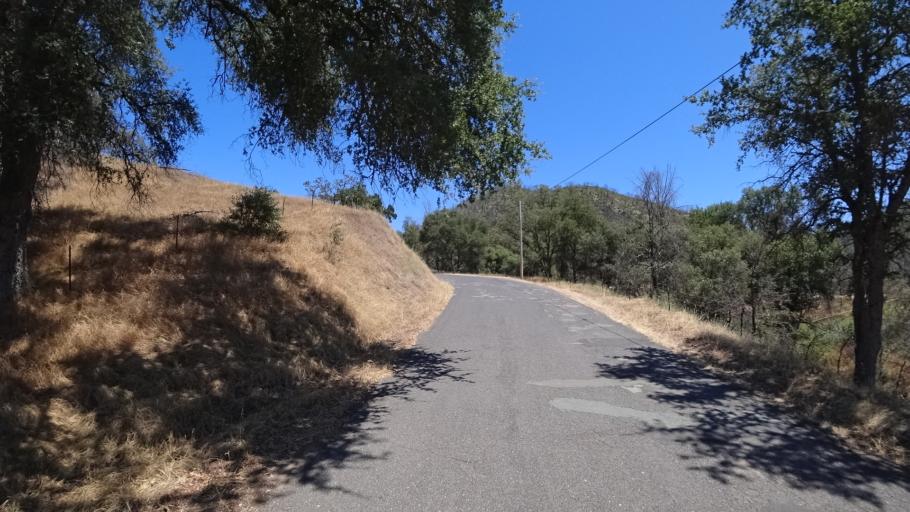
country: US
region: California
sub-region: Calaveras County
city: San Andreas
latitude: 38.2843
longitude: -120.6410
